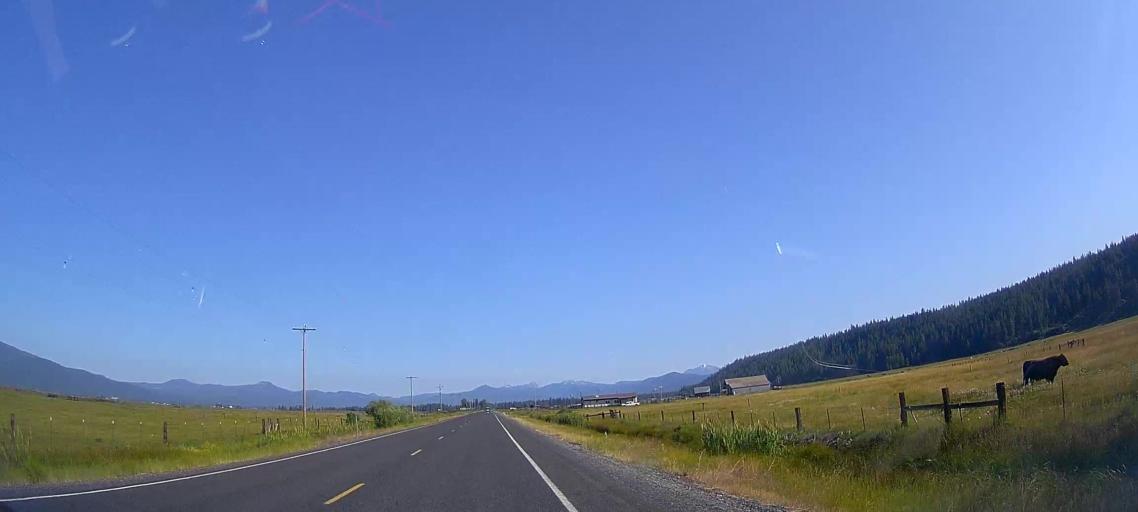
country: US
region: Oregon
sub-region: Klamath County
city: Klamath Falls
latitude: 42.6512
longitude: -121.9565
